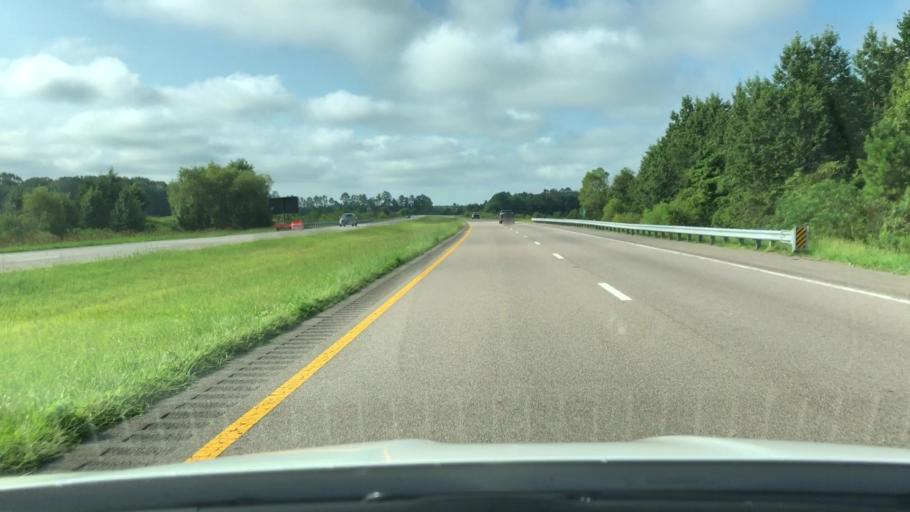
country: US
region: Virginia
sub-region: City of Portsmouth
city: Portsmouth Heights
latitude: 36.6855
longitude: -76.3476
